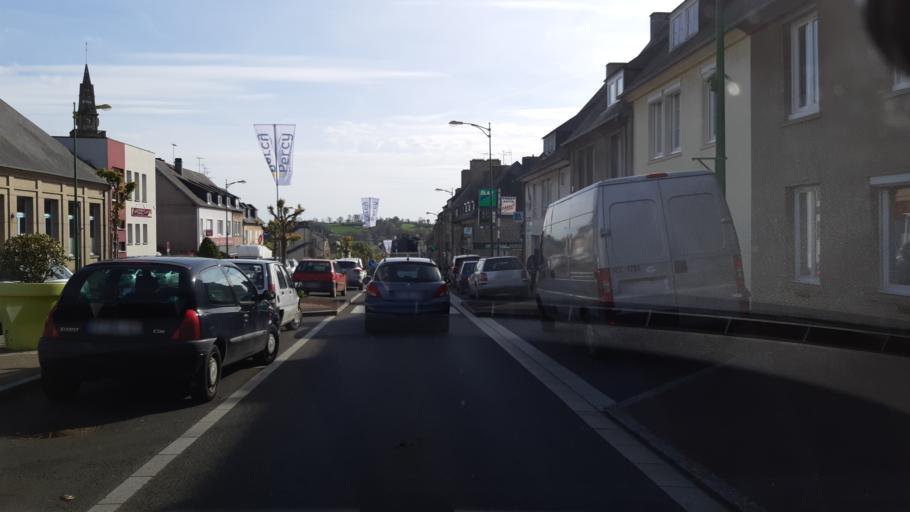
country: FR
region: Lower Normandy
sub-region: Departement de la Manche
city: Percy
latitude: 48.9179
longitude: -1.1901
